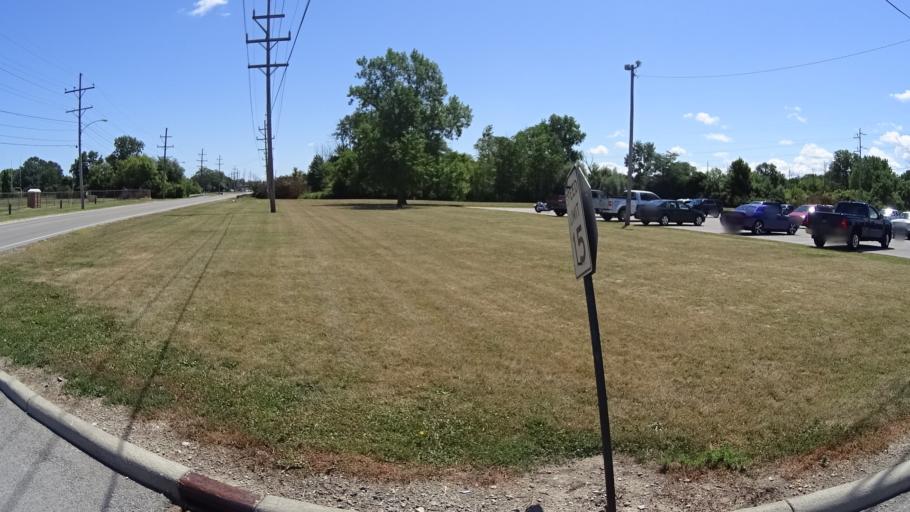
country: US
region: Ohio
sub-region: Erie County
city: Sandusky
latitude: 41.4335
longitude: -82.7342
